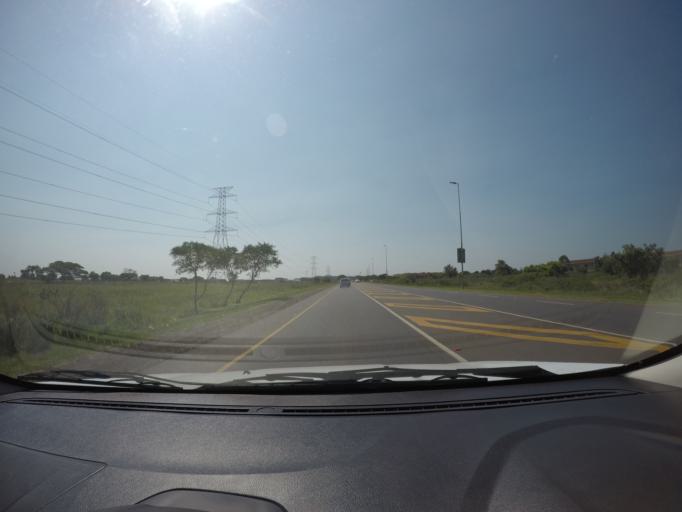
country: ZA
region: KwaZulu-Natal
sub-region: uThungulu District Municipality
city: Richards Bay
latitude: -28.7391
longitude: 32.0459
